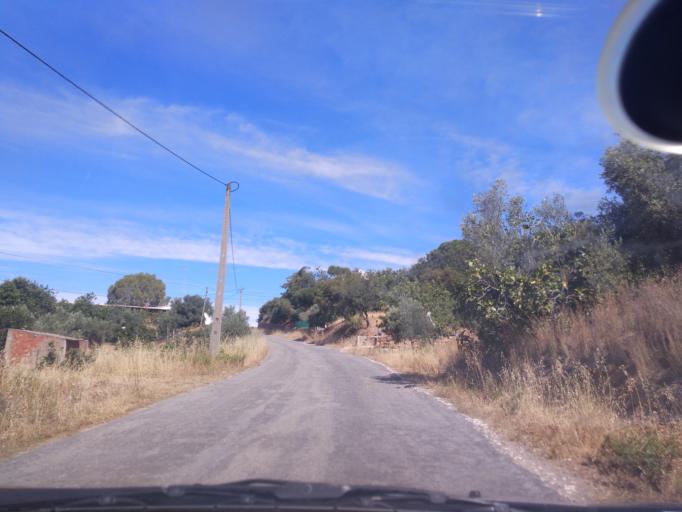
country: PT
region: Faro
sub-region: Olhao
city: Moncarapacho
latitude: 37.1712
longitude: -7.8046
